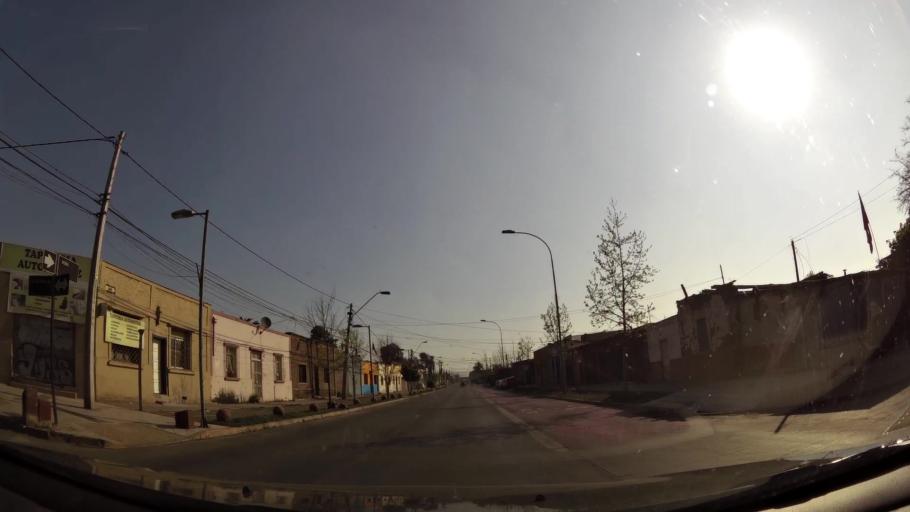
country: CL
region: Santiago Metropolitan
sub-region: Provincia de Santiago
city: Santiago
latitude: -33.4002
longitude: -70.6757
